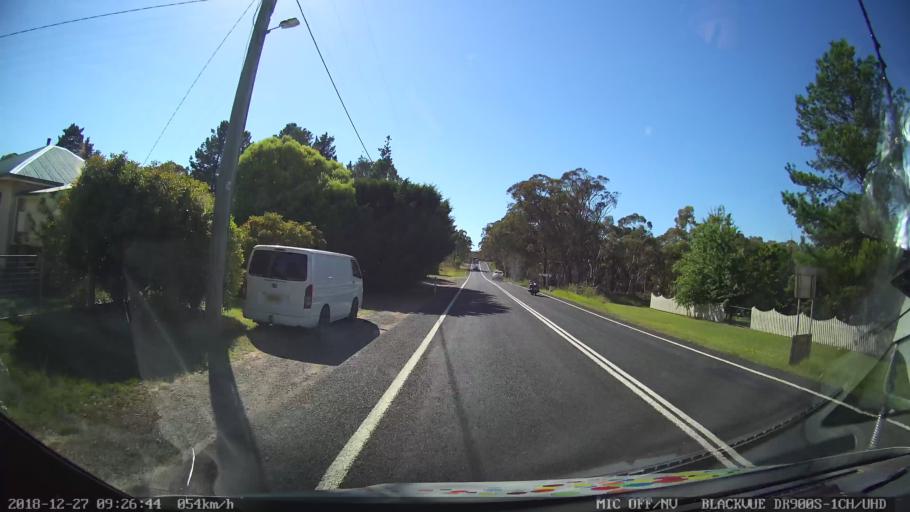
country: AU
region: New South Wales
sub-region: Lithgow
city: Portland
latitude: -33.1476
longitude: 149.9881
